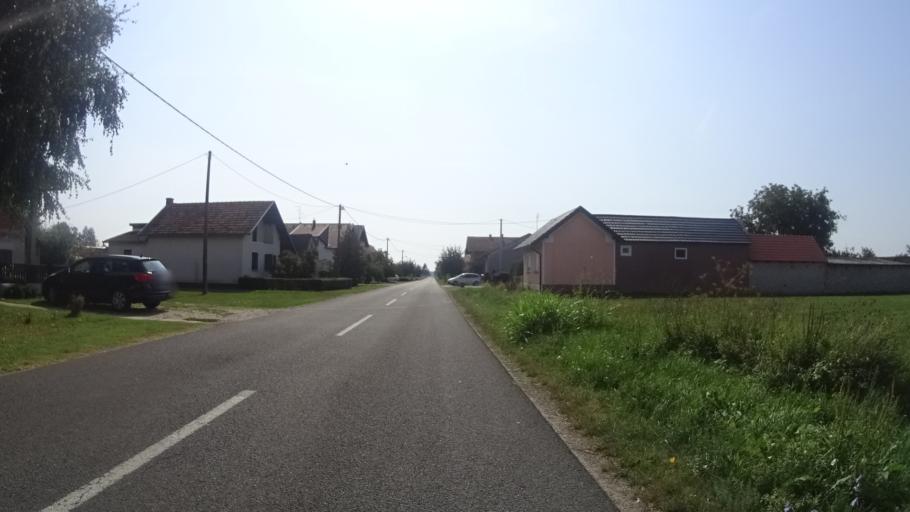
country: HR
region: Medimurska
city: Palovec
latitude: 46.3906
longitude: 16.5377
